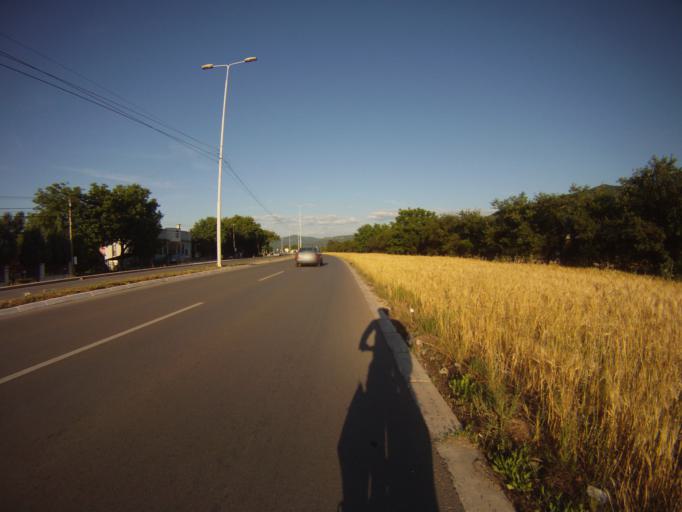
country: RS
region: Central Serbia
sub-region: Nisavski Okrug
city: Niska Banja
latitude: 43.3002
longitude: 21.9947
